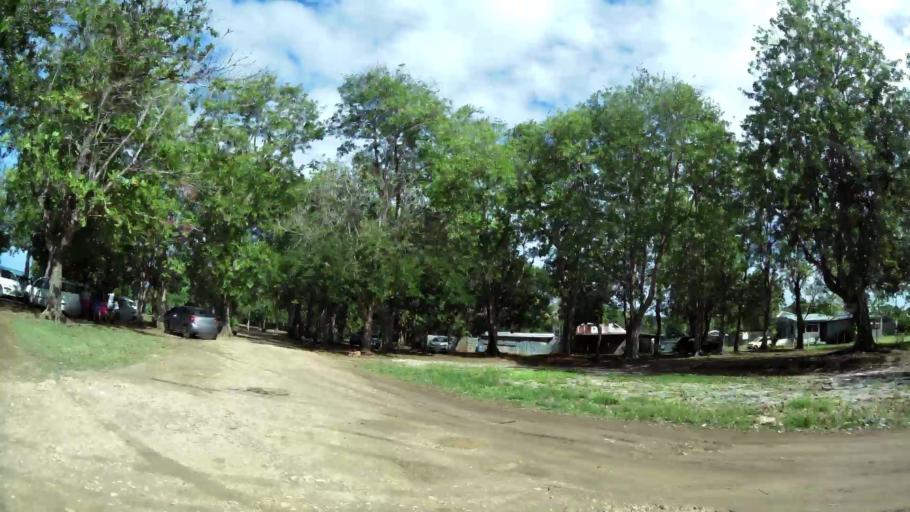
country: GP
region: Guadeloupe
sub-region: Guadeloupe
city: Sainte-Rose
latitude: 16.3557
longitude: -61.7479
